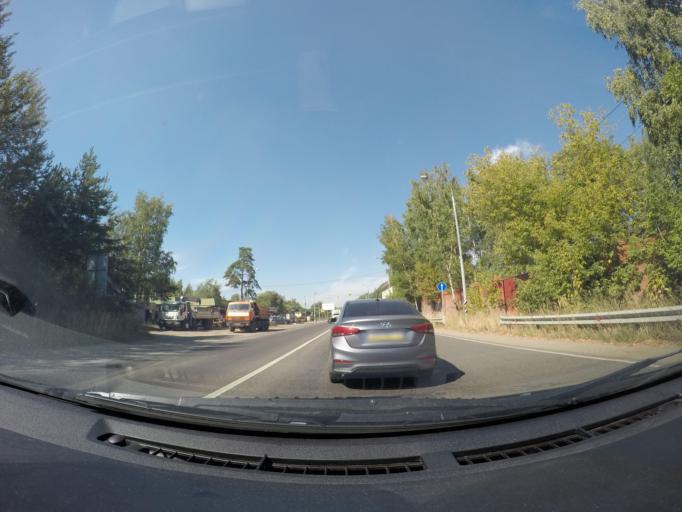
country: RU
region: Moskovskaya
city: Il'inskiy
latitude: 55.6426
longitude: 38.1547
